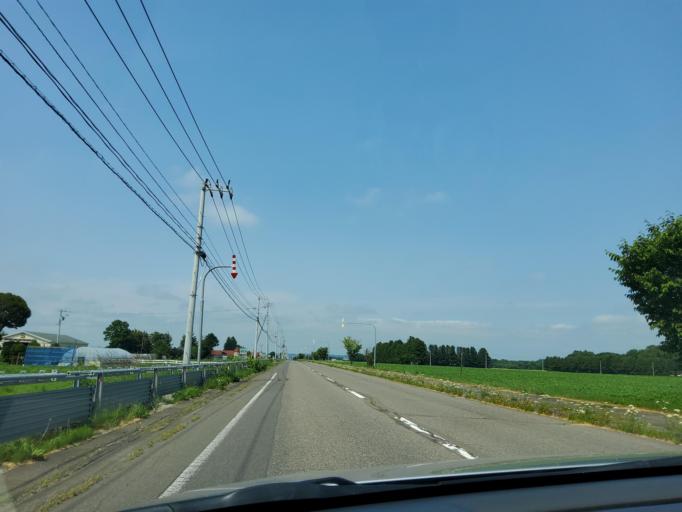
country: JP
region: Hokkaido
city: Obihiro
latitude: 42.8744
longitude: 143.0269
